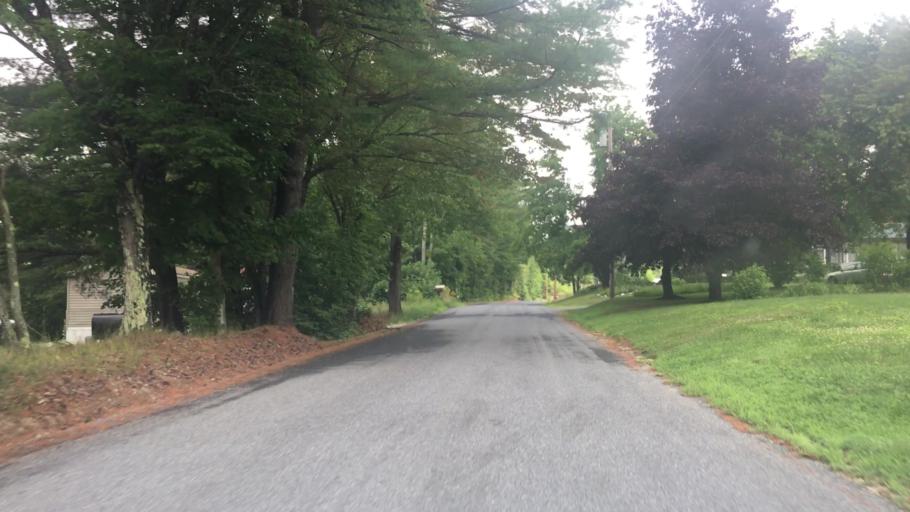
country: US
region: Maine
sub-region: Oxford County
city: Paris
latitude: 44.2863
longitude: -70.5211
